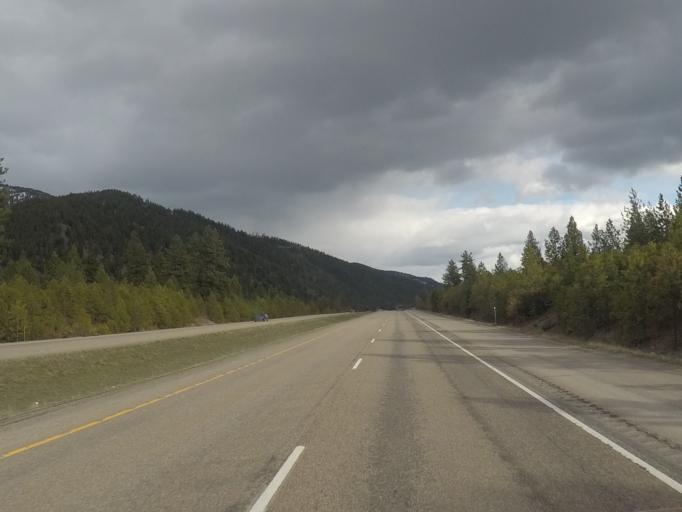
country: US
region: Montana
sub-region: Missoula County
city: Bonner-West Riverside
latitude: 46.8674
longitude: -113.8782
